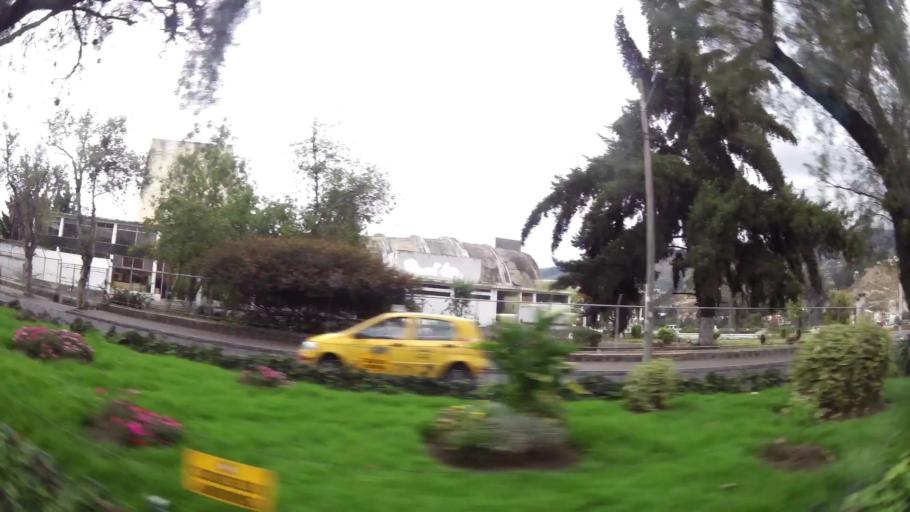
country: EC
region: Tungurahua
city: Ambato
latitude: -1.2322
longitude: -78.6242
